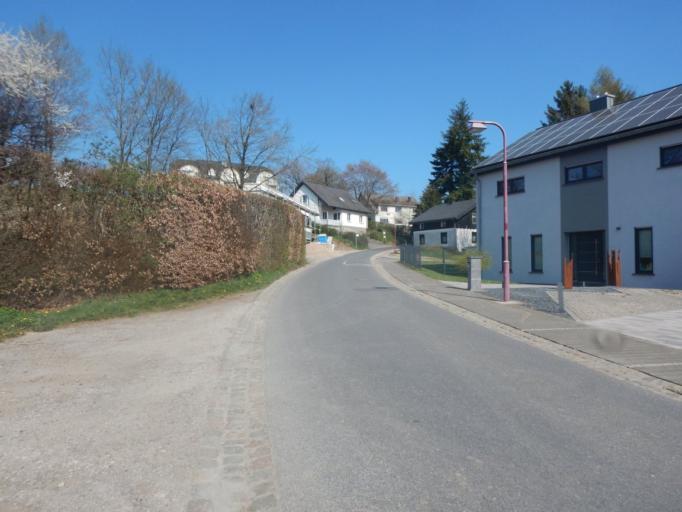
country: LU
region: Diekirch
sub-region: Canton de Clervaux
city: Clervaux
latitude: 50.0596
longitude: 6.0008
